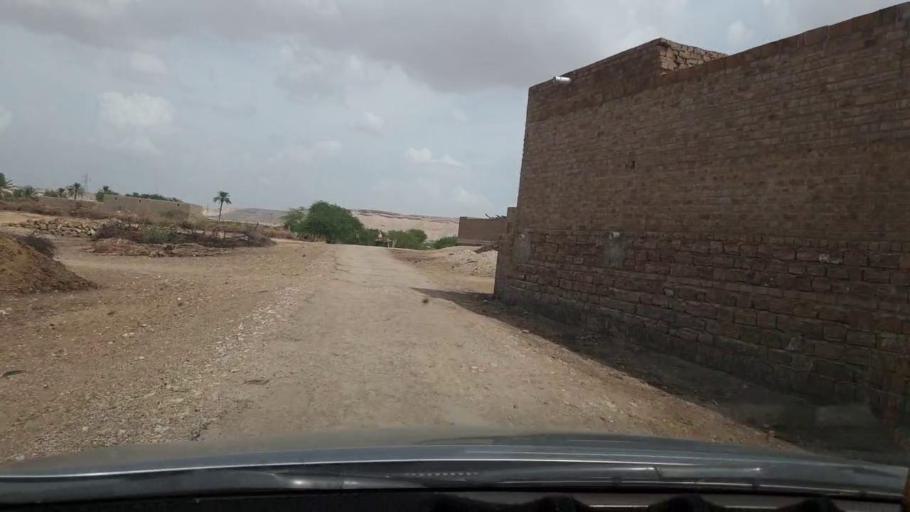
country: PK
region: Sindh
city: Khairpur
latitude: 27.4776
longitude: 68.8573
